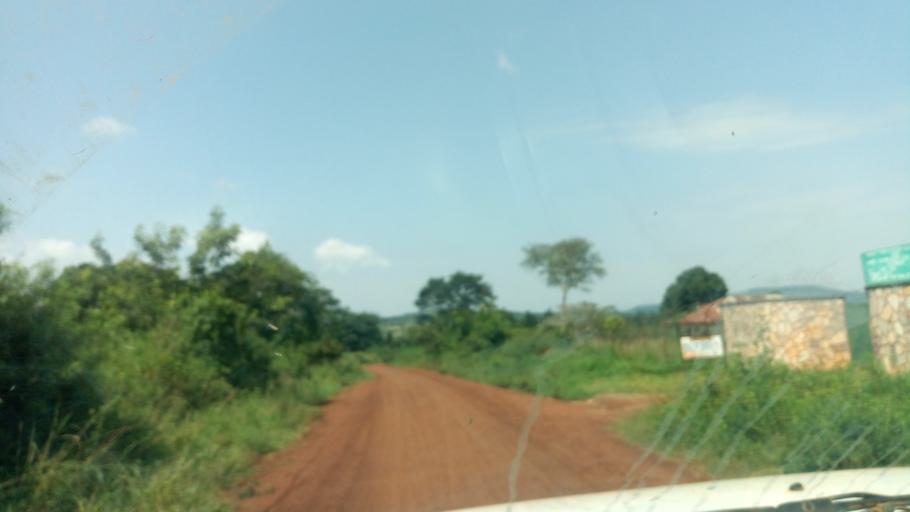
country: UG
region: Western Region
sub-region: Masindi District
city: Masindi
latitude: 1.6755
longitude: 31.8291
